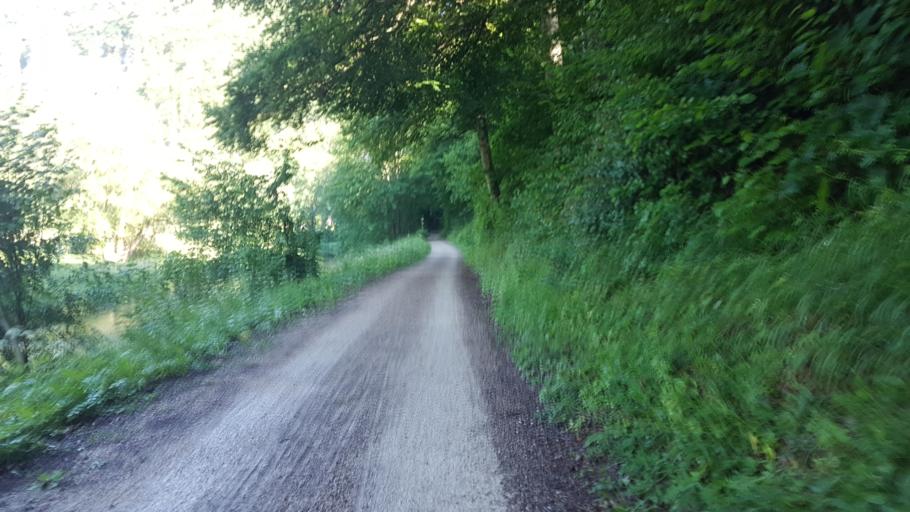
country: DE
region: Baden-Wuerttemberg
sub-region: Tuebingen Region
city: Stetten am Kalten Markt
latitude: 48.0805
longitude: 9.0806
